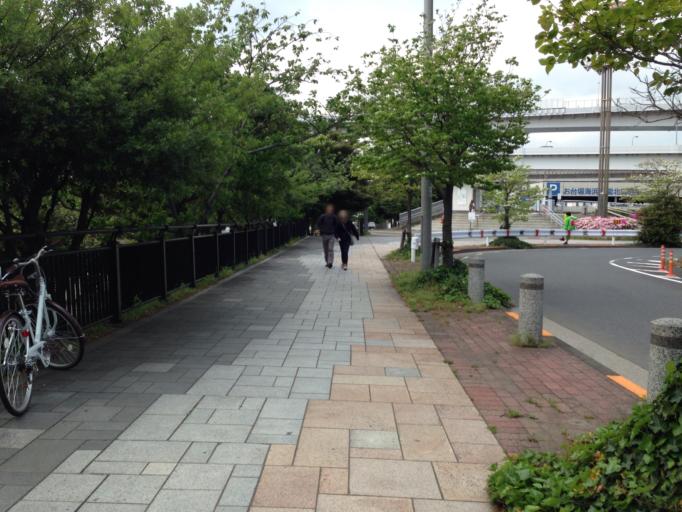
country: JP
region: Tokyo
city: Tokyo
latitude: 35.6347
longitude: 139.7758
